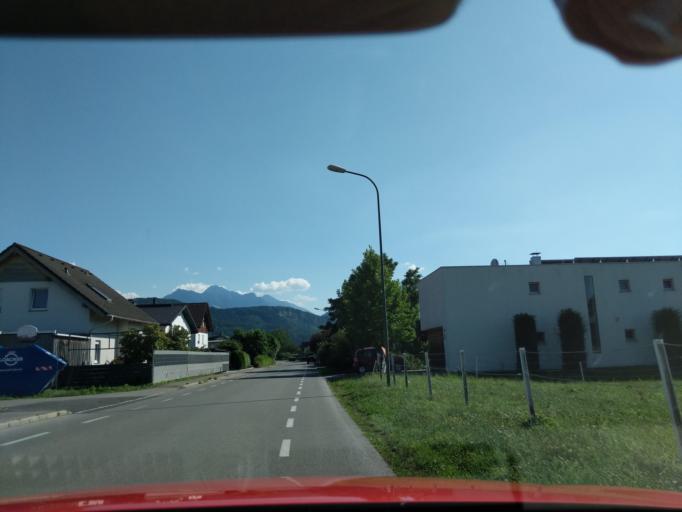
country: AT
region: Vorarlberg
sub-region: Politischer Bezirk Feldkirch
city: Rankweil
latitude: 47.2777
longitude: 9.6312
